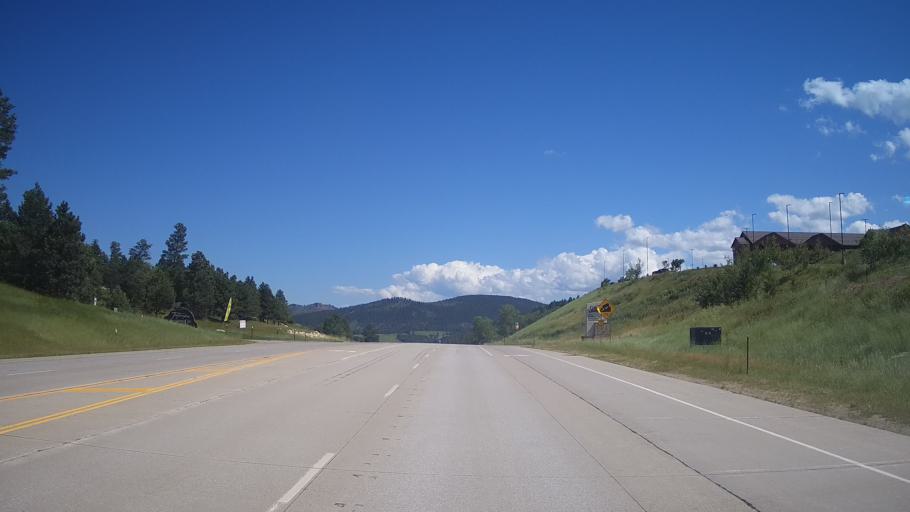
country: US
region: South Dakota
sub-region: Lawrence County
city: Deadwood
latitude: 44.3970
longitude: -103.7161
